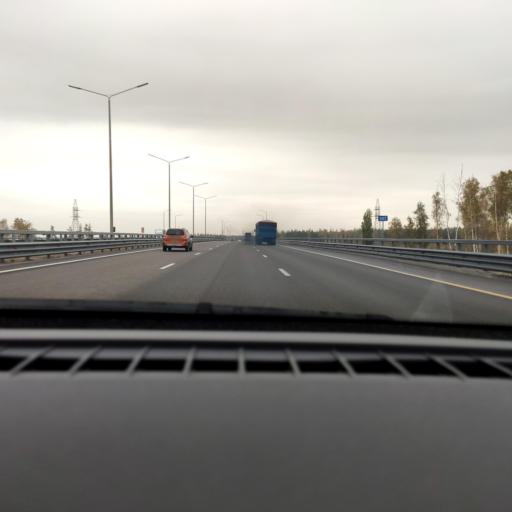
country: RU
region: Voronezj
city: Somovo
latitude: 51.7367
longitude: 39.3091
